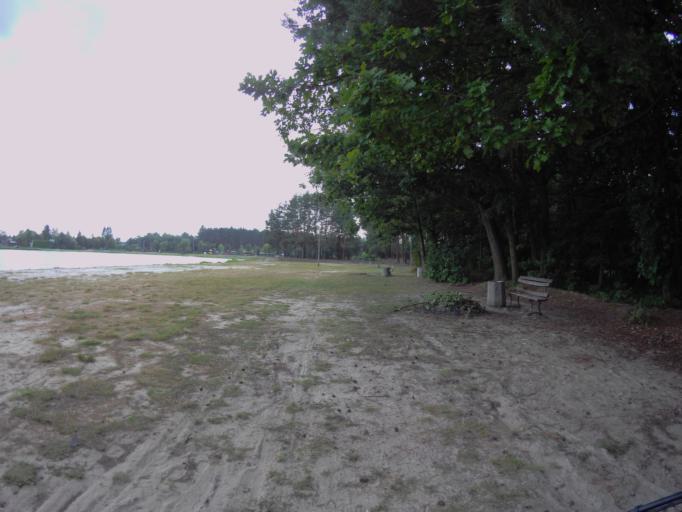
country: PL
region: Subcarpathian Voivodeship
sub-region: Powiat lezajski
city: Brzoza Krolewska
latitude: 50.2394
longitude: 22.3210
